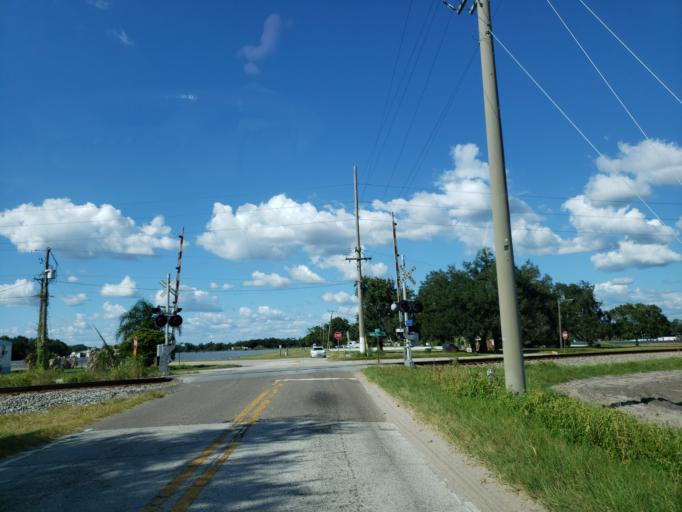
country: US
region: Florida
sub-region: Hillsborough County
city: Dover
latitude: 27.9664
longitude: -82.2031
